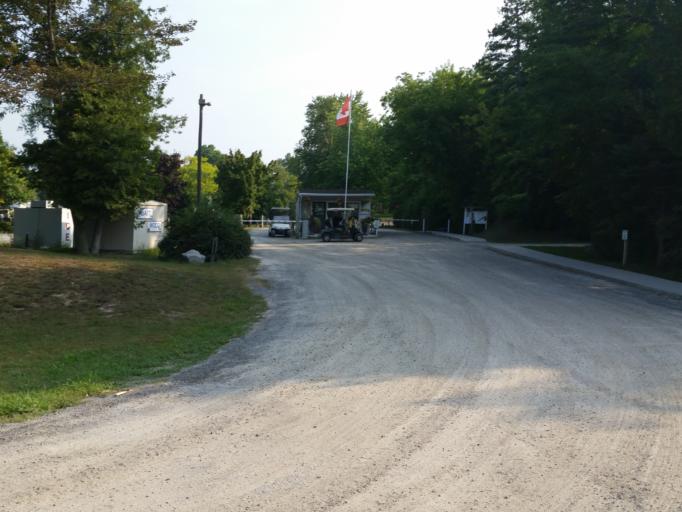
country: CA
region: Ontario
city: Prince Edward
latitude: 43.9016
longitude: -77.2274
